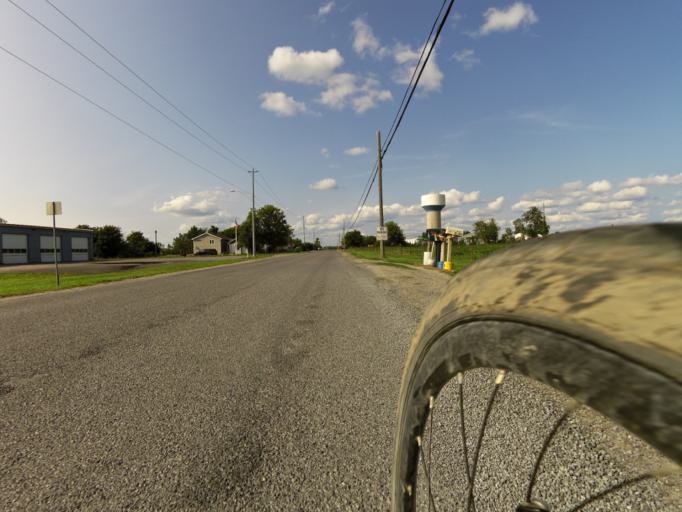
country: CA
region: Ontario
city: Kingston
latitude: 44.4016
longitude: -76.5963
